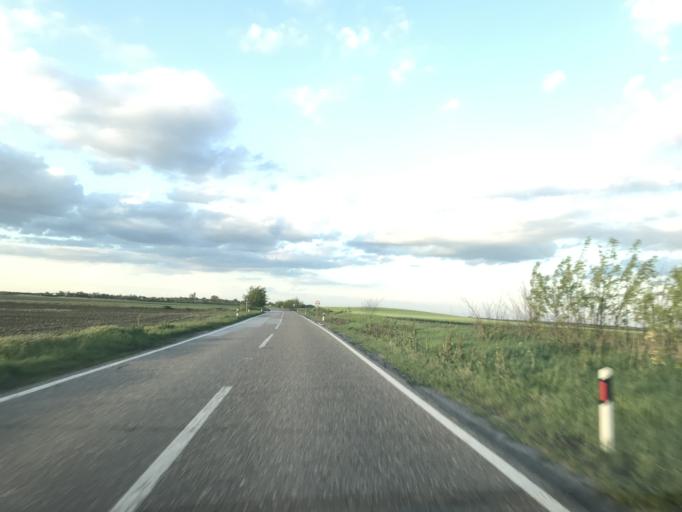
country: RS
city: Cestereg
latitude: 45.5483
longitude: 20.5131
